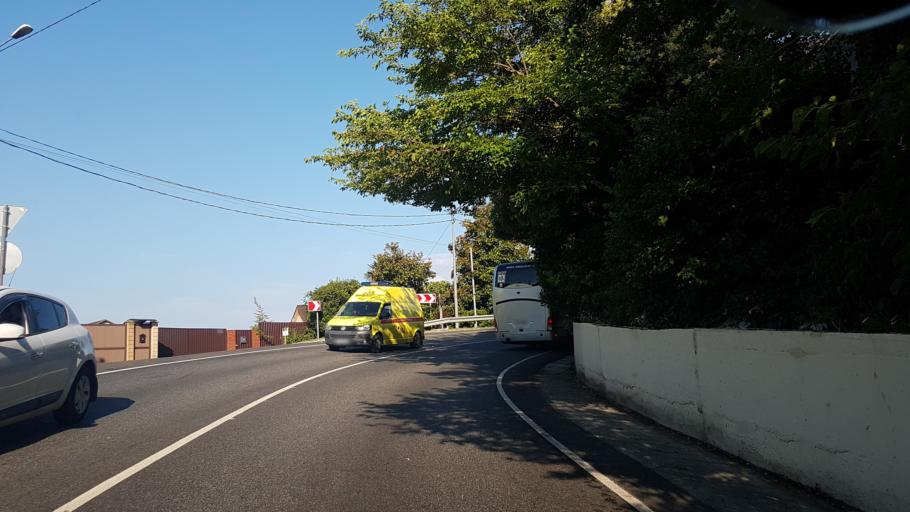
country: RU
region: Krasnodarskiy
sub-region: Sochi City
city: Lazarevskoye
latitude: 43.8517
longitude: 39.4069
